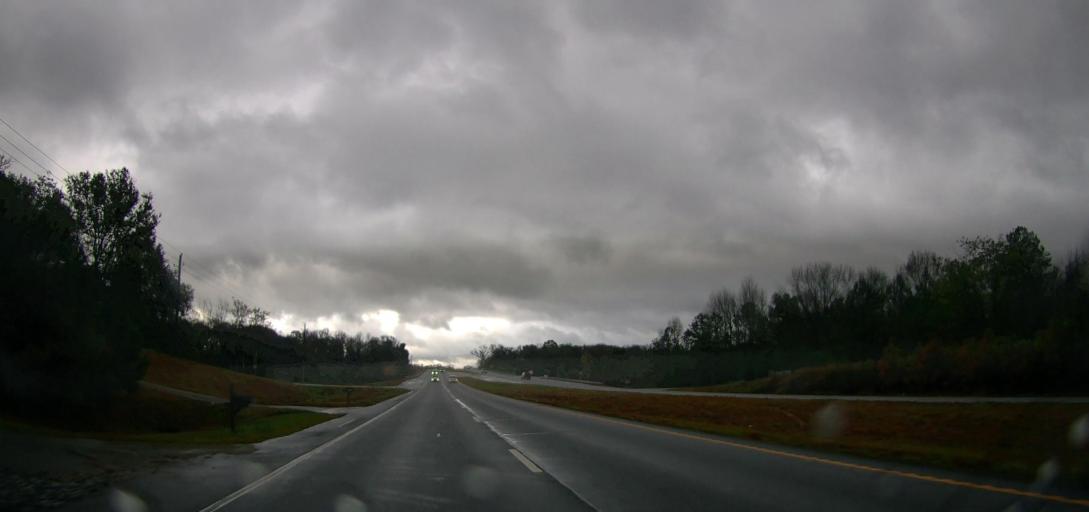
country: US
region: Georgia
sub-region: Jackson County
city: Nicholson
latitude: 34.1383
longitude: -83.4322
